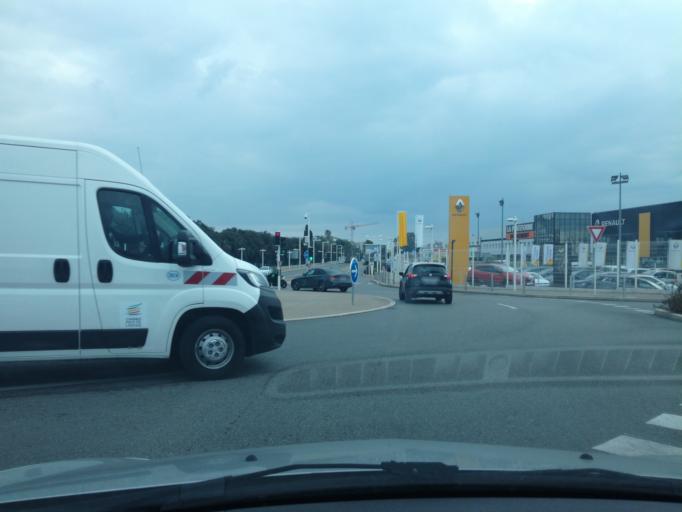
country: FR
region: Provence-Alpes-Cote d'Azur
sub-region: Departement des Alpes-Maritimes
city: Mandelieu-la-Napoule
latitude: 43.5500
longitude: 6.9620
